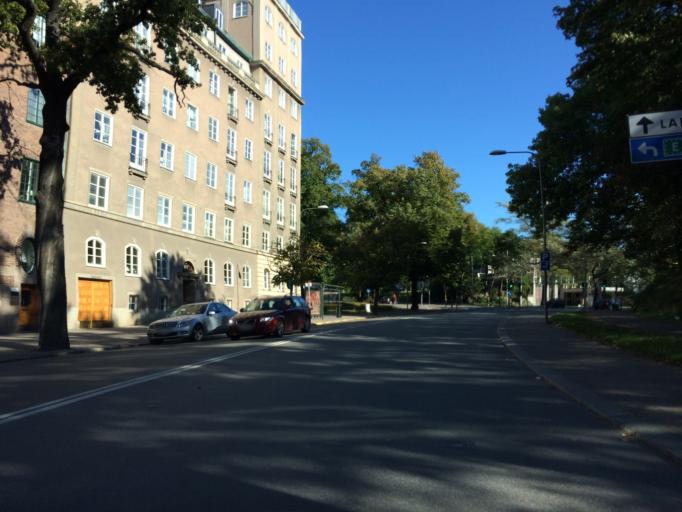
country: SE
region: Stockholm
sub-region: Stockholms Kommun
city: OEstermalm
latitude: 59.3328
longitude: 18.0975
